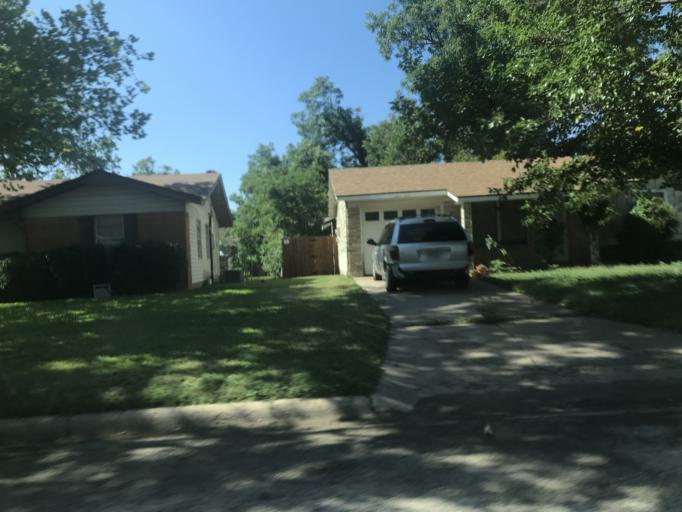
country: US
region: Texas
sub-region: Taylor County
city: Abilene
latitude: 32.4090
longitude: -99.7491
